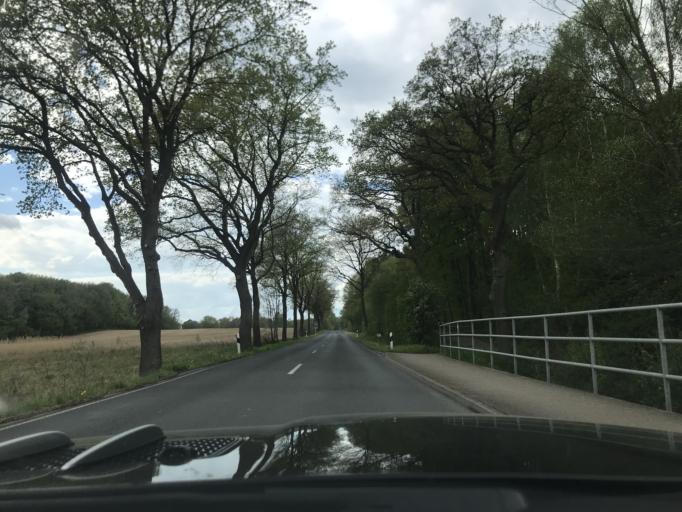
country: DE
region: Schleswig-Holstein
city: Gross Gronau
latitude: 53.7845
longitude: 10.7630
